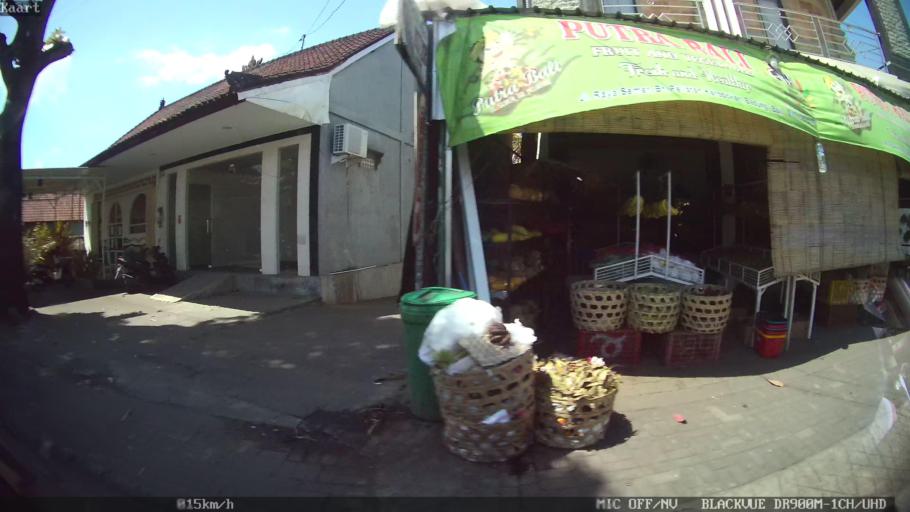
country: ID
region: Bali
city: Banjar Gunungpande
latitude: -8.6518
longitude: 115.1623
